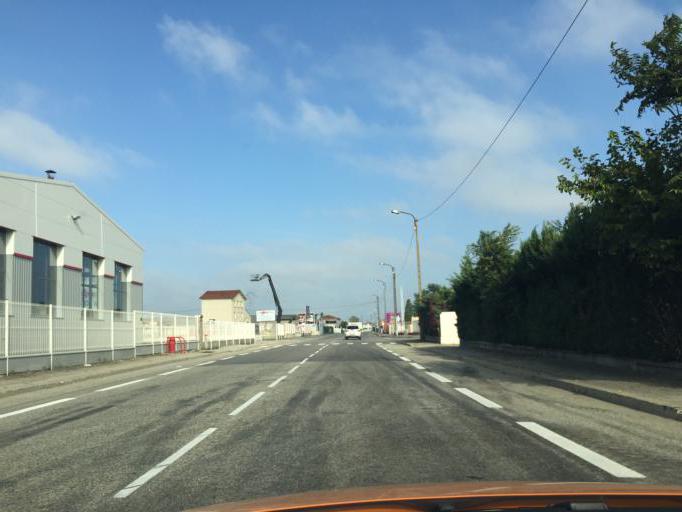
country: FR
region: Rhone-Alpes
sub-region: Departement de la Drome
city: Portes-les-Valence
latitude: 44.8973
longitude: 4.8837
